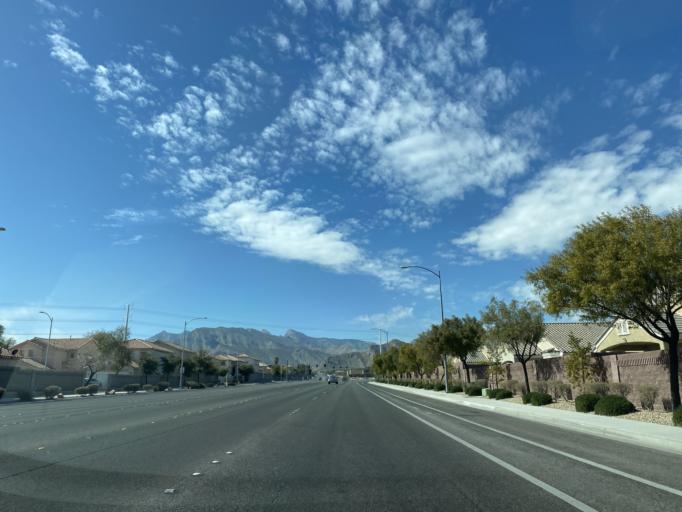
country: US
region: Nevada
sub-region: Clark County
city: Summerlin South
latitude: 36.2337
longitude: -115.2760
